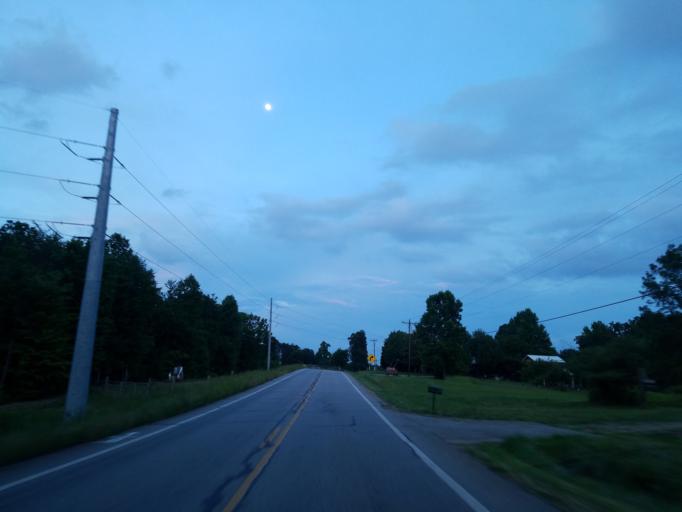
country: US
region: Georgia
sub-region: Dawson County
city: Dawsonville
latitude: 34.4448
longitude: -84.1648
